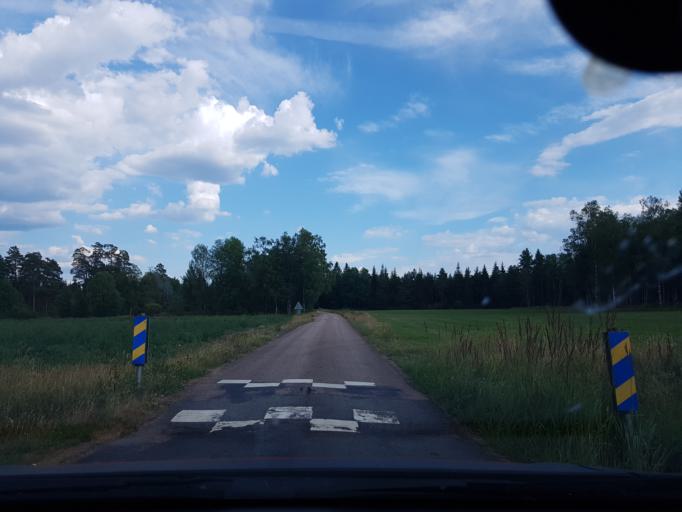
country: SE
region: Joenkoeping
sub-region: Gislaveds Kommun
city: Reftele
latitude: 57.2123
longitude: 13.5805
